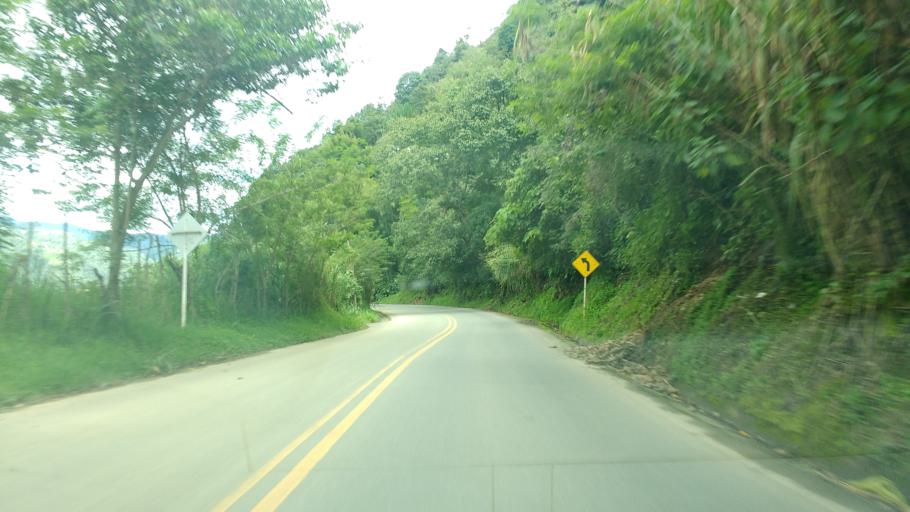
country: CO
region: Antioquia
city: Amaga
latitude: 6.0516
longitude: -75.7241
